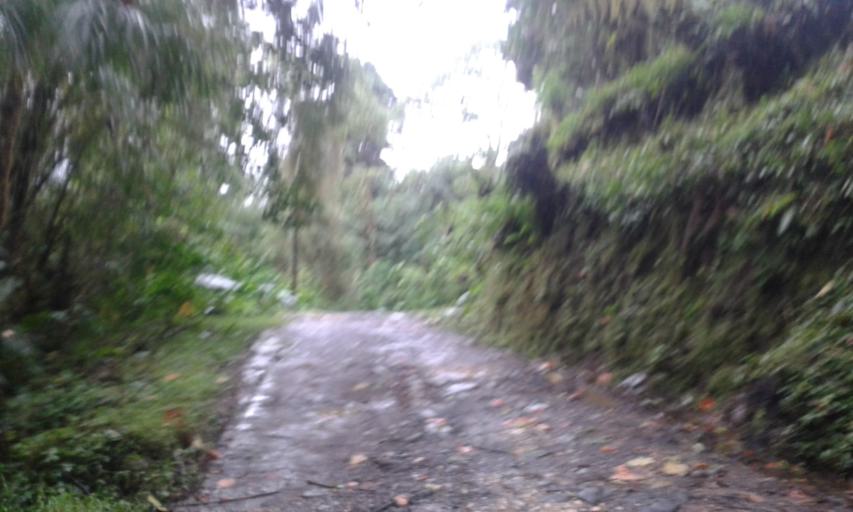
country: CR
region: San Jose
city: Ipis
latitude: 10.0310
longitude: -83.9346
